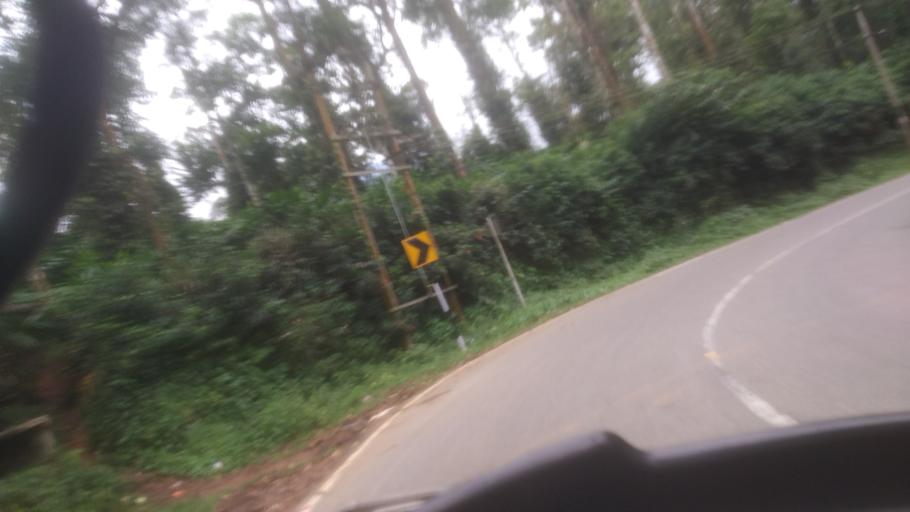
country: IN
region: Tamil Nadu
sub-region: Theni
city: Kombai
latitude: 9.8964
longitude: 77.1914
